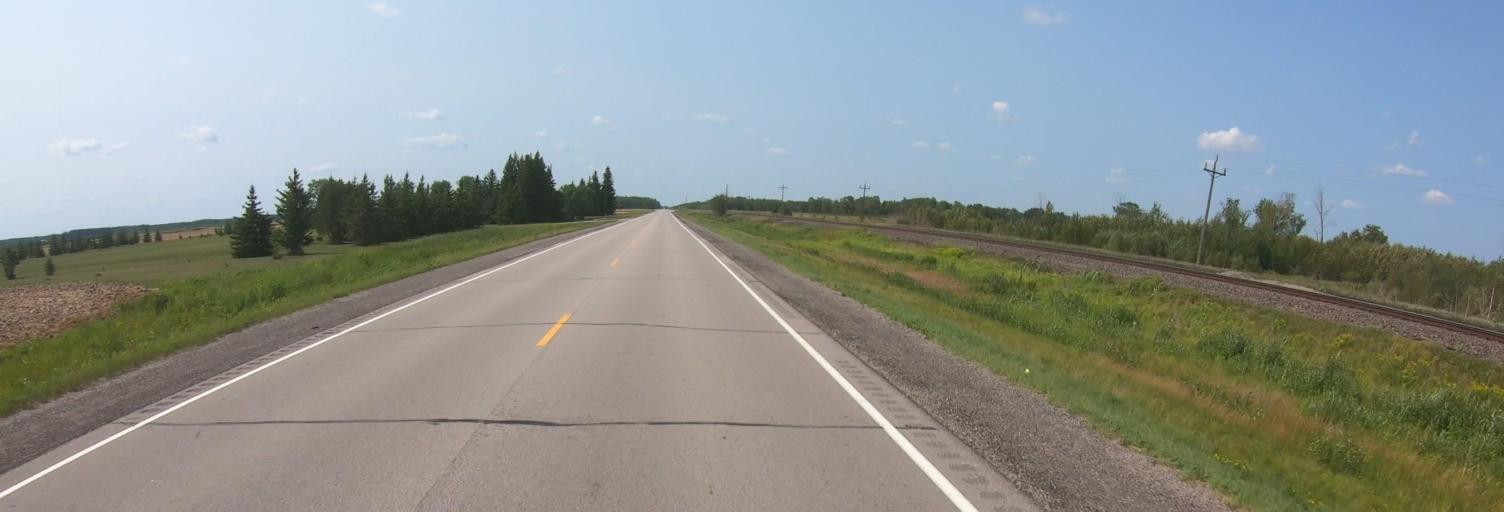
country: US
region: Minnesota
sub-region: Lake of the Woods County
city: Baudette
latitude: 48.7209
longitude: -94.7541
